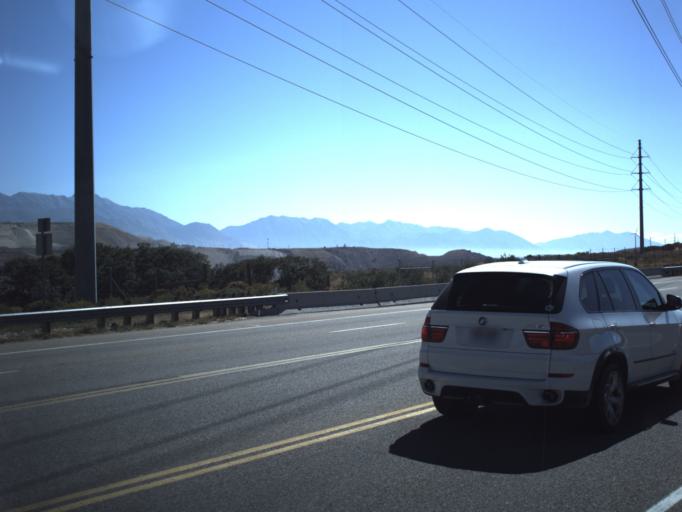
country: US
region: Utah
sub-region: Salt Lake County
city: Bluffdale
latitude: 40.4615
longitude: -111.9424
